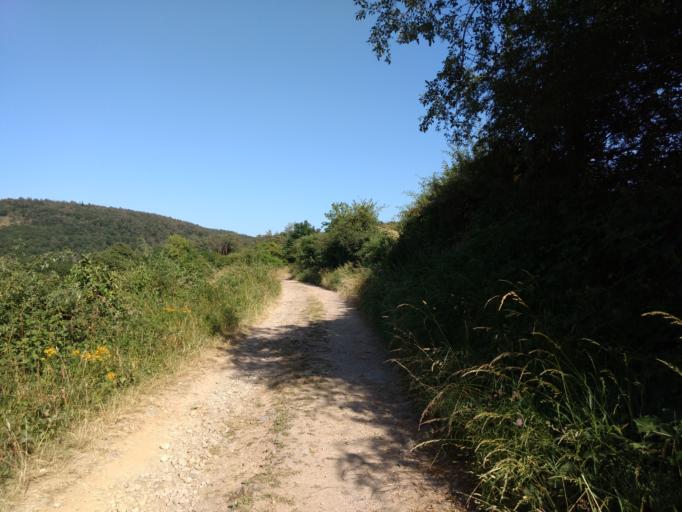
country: FR
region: Midi-Pyrenees
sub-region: Departement de l'Aveyron
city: La Loubiere
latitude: 44.3620
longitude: 2.6865
